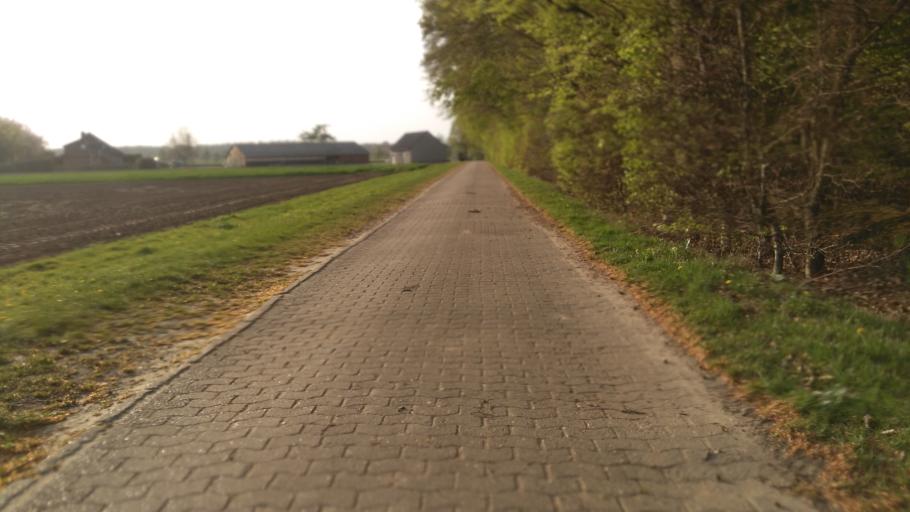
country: DE
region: Lower Saxony
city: Apensen
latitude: 53.4671
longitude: 9.6374
